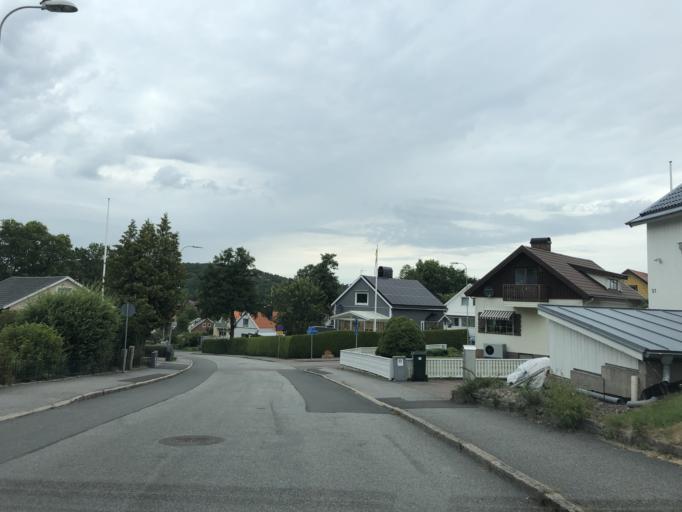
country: SE
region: Vaestra Goetaland
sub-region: Goteborg
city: Majorna
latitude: 57.7258
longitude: 11.9246
